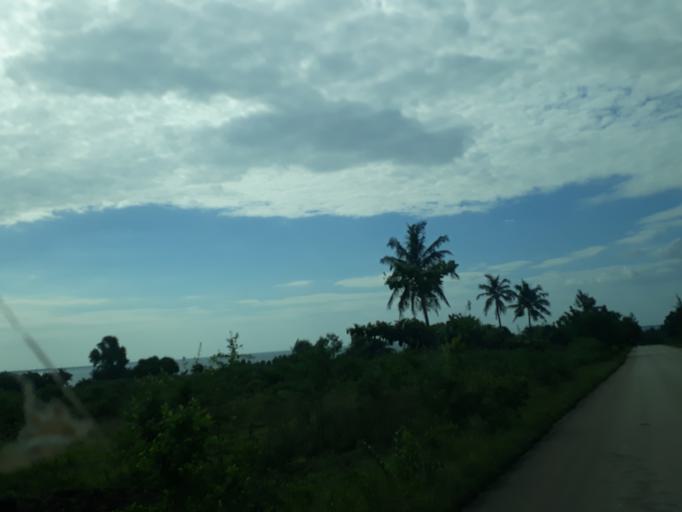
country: TZ
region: Zanzibar North
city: Kijini
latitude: -5.8446
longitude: 39.2839
